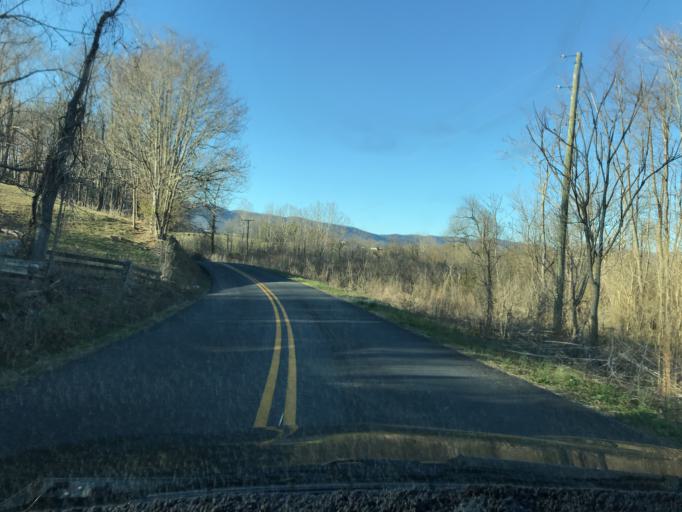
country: US
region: Virginia
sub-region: Botetourt County
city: Blue Ridge
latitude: 37.4028
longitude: -79.7024
